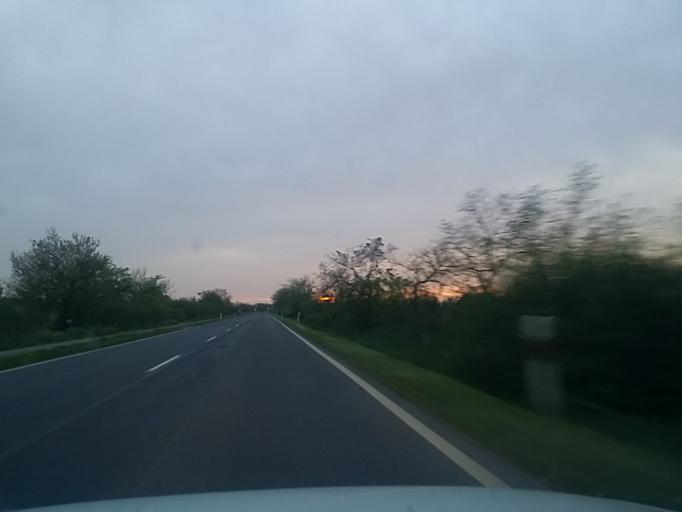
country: HU
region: Bekes
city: Mezobereny
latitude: 46.7127
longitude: 20.9524
